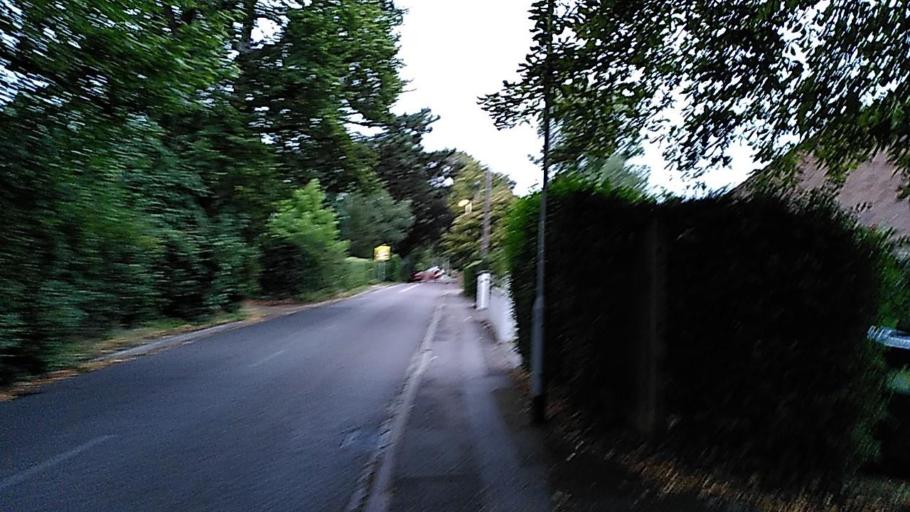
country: GB
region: England
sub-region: Reading
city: Reading
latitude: 51.4832
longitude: -0.9725
